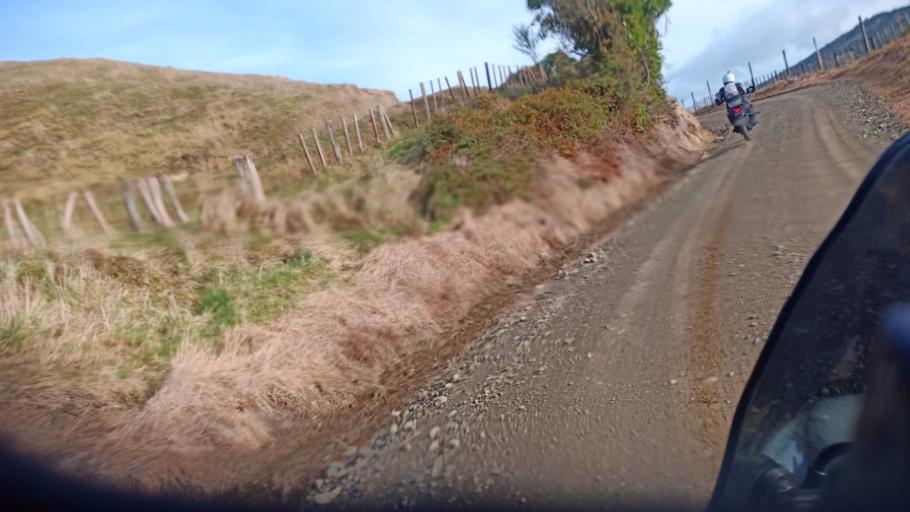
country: NZ
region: Bay of Plenty
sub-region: Opotiki District
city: Opotiki
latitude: -38.4477
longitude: 177.5398
